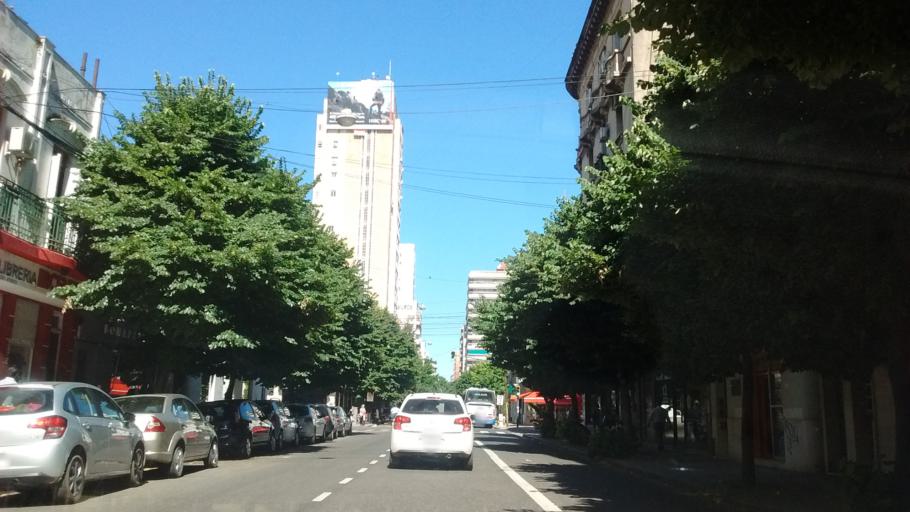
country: AR
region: Santa Fe
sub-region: Departamento de Rosario
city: Rosario
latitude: -32.9434
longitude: -60.6554
